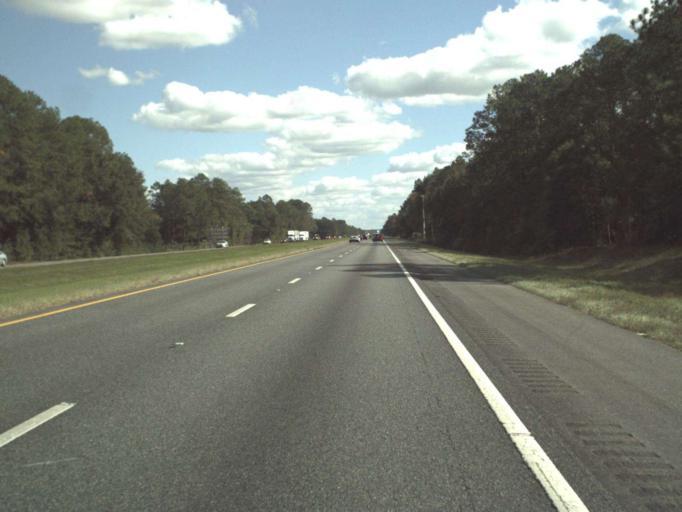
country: US
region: Florida
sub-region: Jackson County
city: Marianna
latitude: 30.7089
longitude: -85.1506
